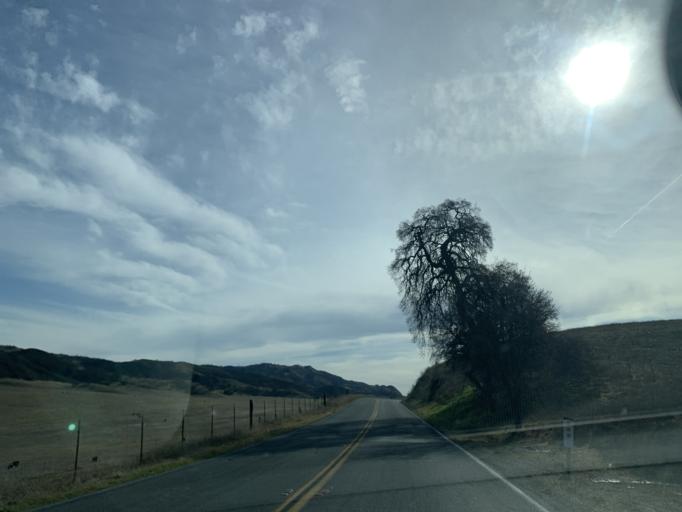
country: US
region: California
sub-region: Monterey County
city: Greenfield
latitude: 36.4917
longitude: -121.0781
